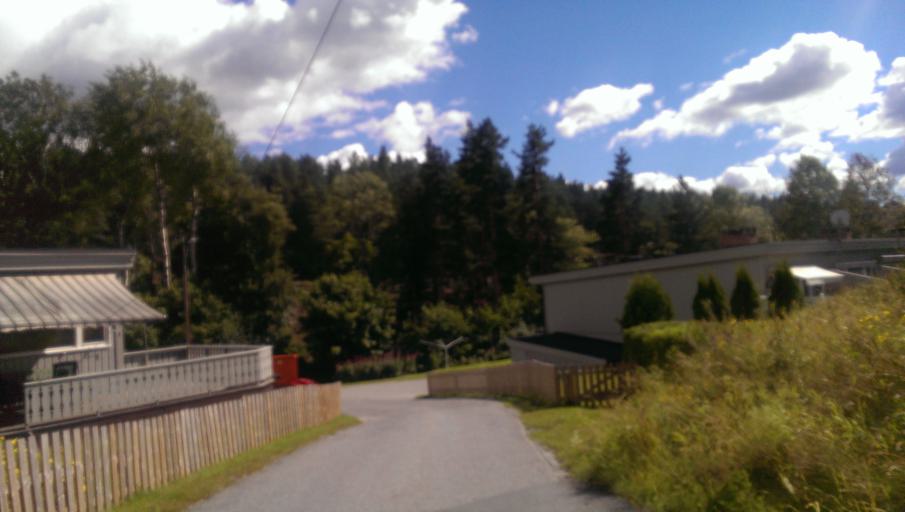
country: NO
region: Buskerud
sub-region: Kongsberg
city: Kongsberg
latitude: 59.6562
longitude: 9.6563
